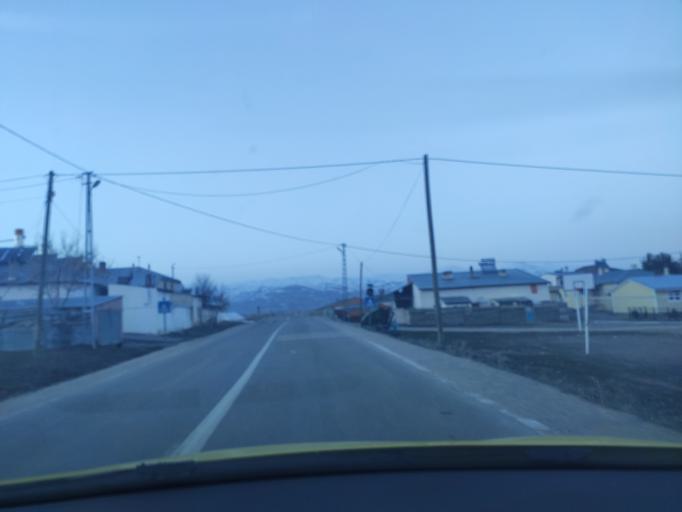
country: TR
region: Bayburt
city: Aydintepe
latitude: 40.3178
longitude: 40.1252
